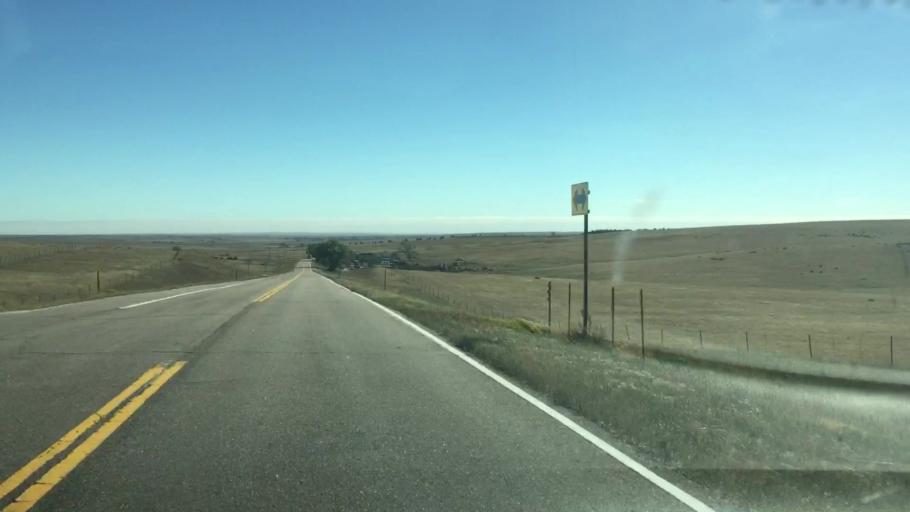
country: US
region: Colorado
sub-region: Lincoln County
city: Limon
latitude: 39.2881
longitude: -103.9671
